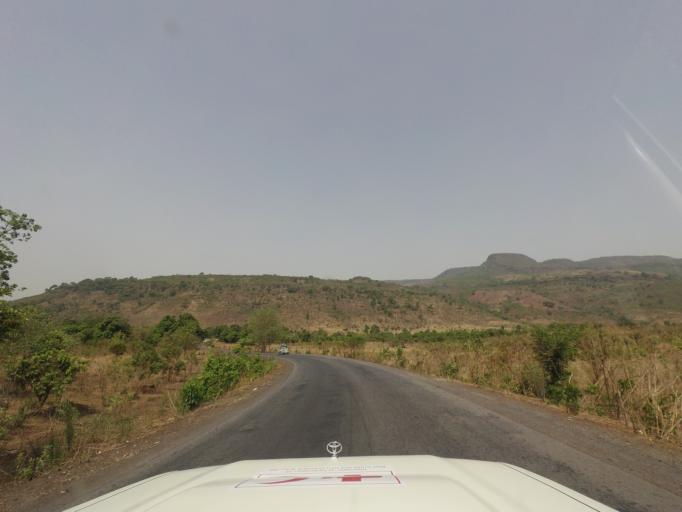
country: GN
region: Mamou
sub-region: Mamou Prefecture
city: Mamou
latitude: 10.2103
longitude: -12.4618
